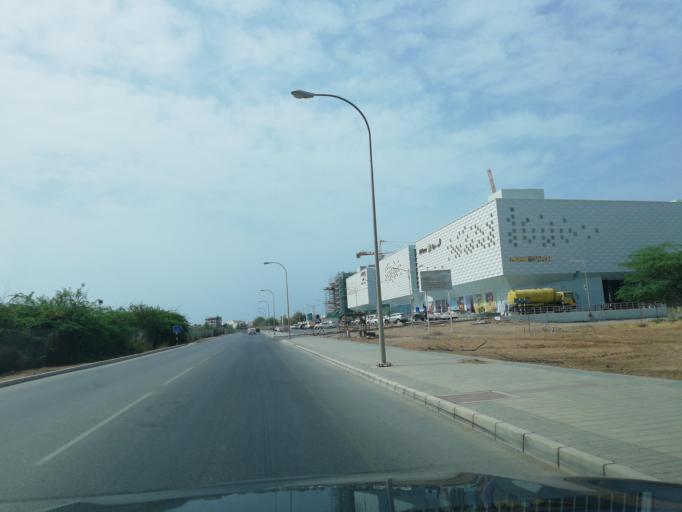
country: OM
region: Muhafazat Masqat
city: As Sib al Jadidah
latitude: 23.6211
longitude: 58.2498
